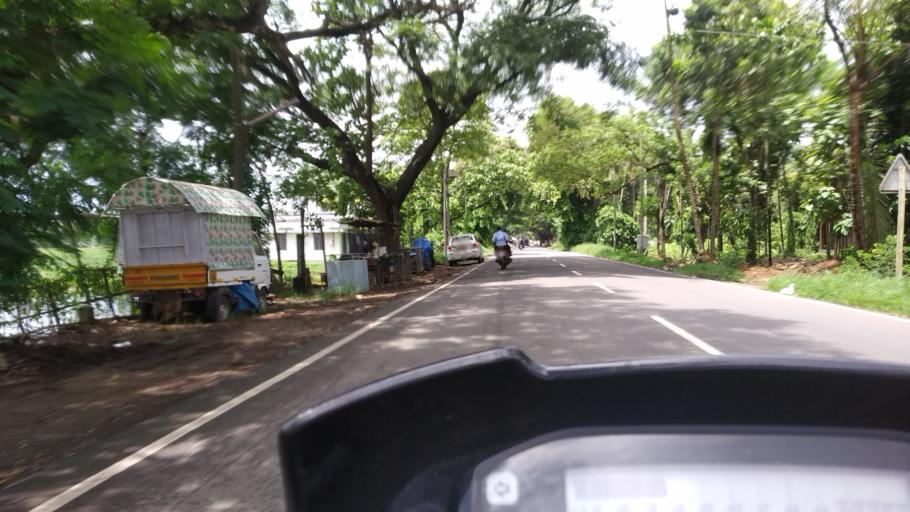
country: IN
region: Kerala
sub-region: Ernakulam
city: Elur
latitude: 10.1307
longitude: 76.2880
